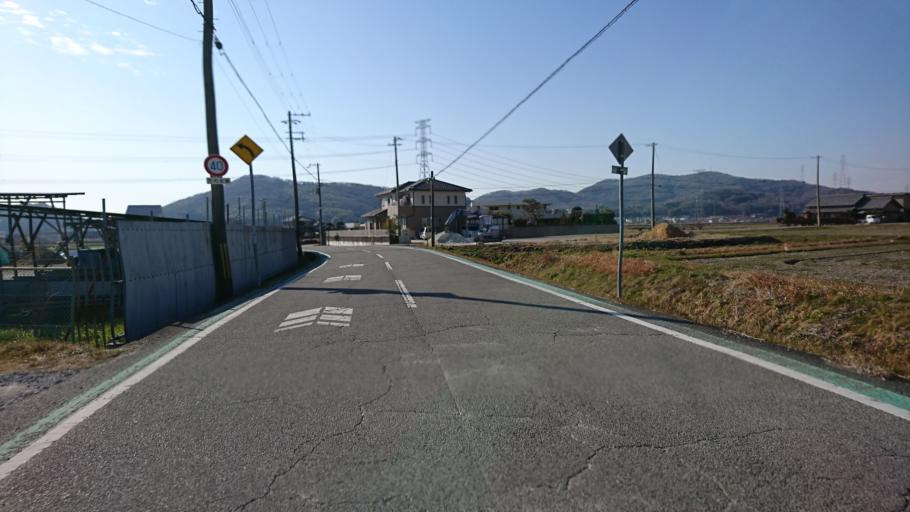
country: JP
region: Hyogo
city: Kakogawacho-honmachi
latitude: 34.8325
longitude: 134.8369
